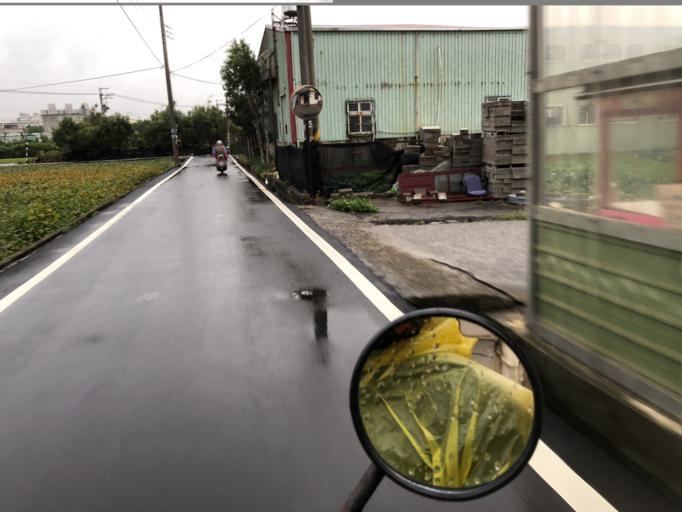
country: TW
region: Taiwan
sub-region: Hsinchu
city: Zhubei
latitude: 24.8497
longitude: 120.9921
